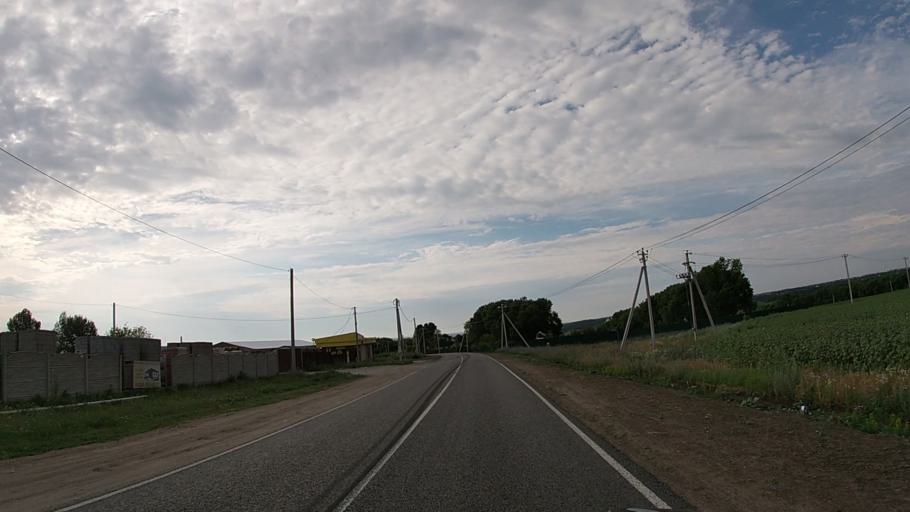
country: RU
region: Belgorod
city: Severnyy
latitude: 50.7200
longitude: 36.5856
